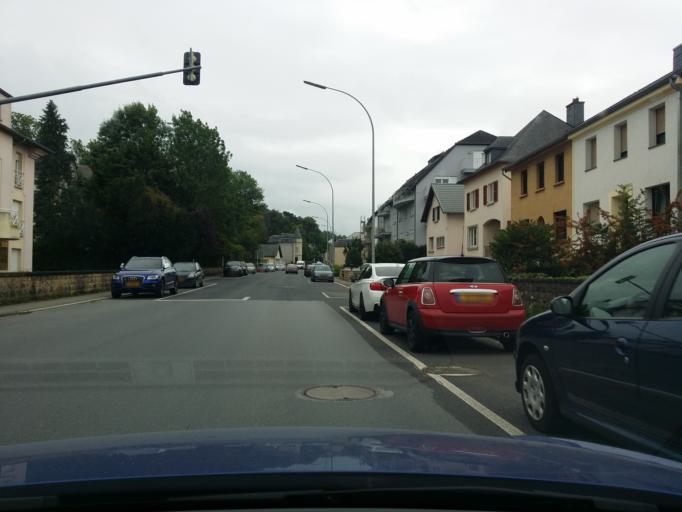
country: LU
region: Luxembourg
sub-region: Canton de Mersch
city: Mersch
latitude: 49.7467
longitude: 6.1115
